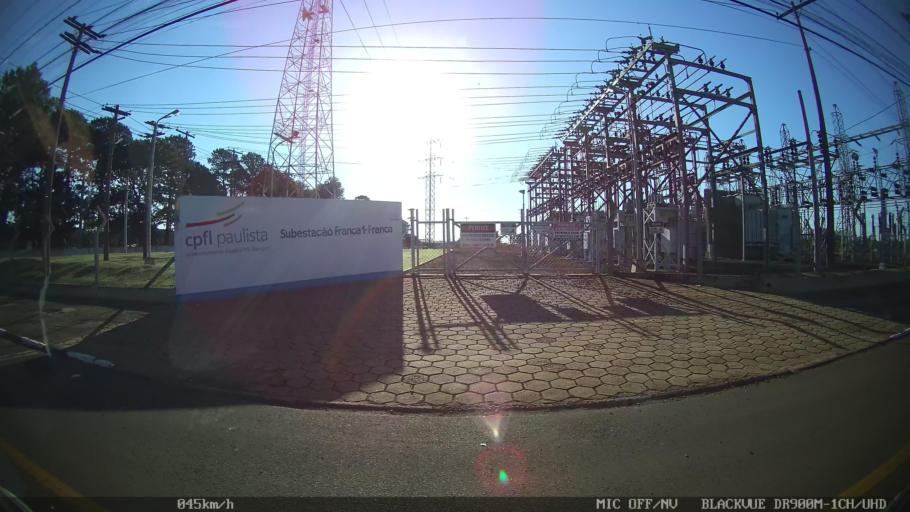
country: BR
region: Sao Paulo
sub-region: Franca
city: Franca
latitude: -20.5158
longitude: -47.3798
